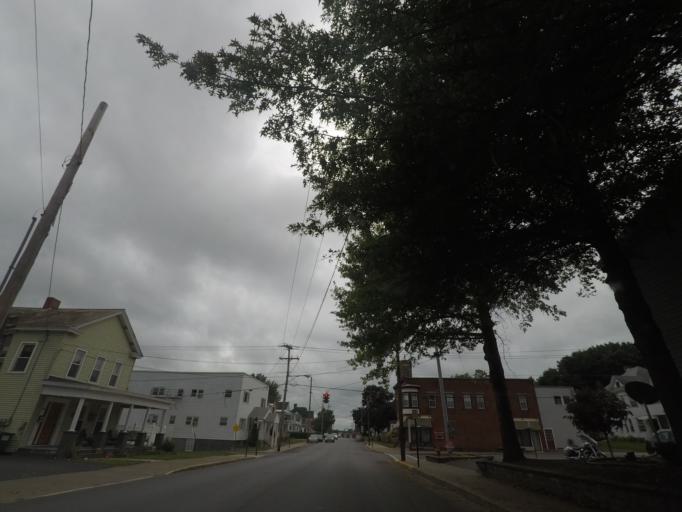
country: US
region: New York
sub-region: Saratoga County
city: Mechanicville
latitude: 42.9082
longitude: -73.6839
